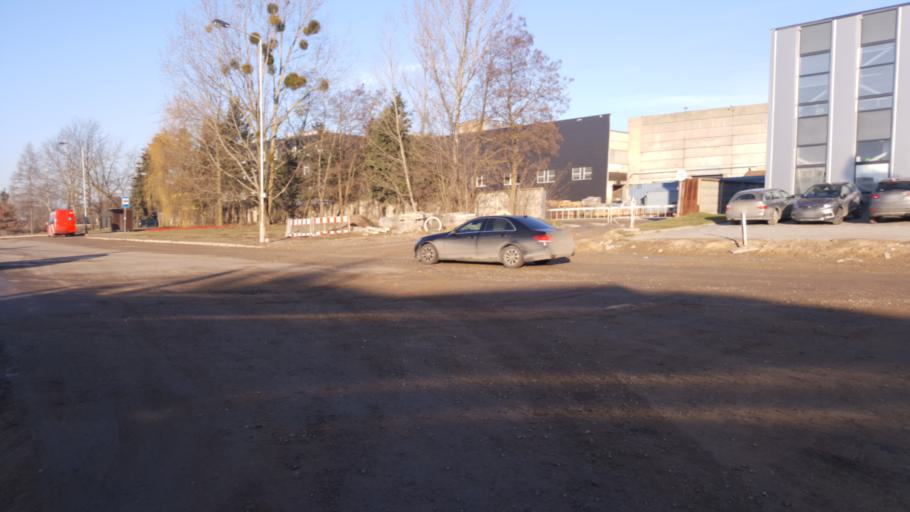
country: LT
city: Ramuciai
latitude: 54.9010
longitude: 24.0297
